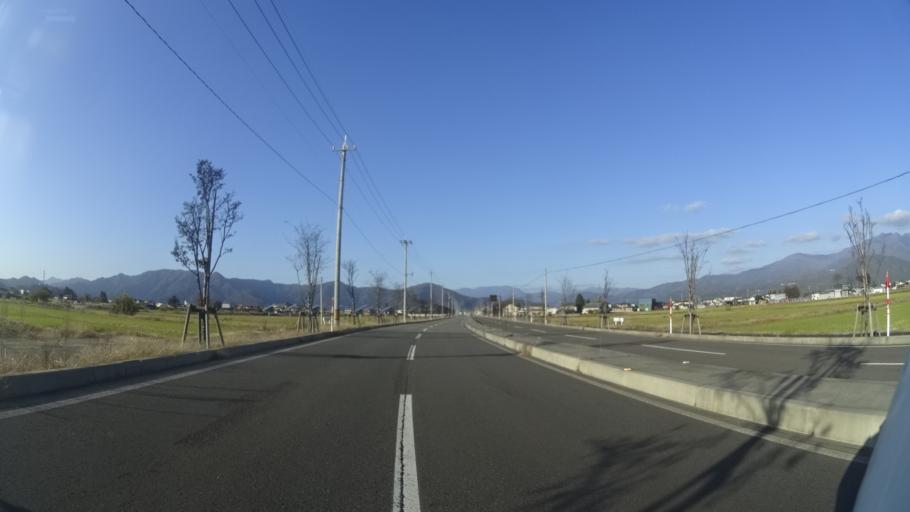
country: JP
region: Fukui
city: Ono
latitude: 35.9758
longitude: 136.5118
